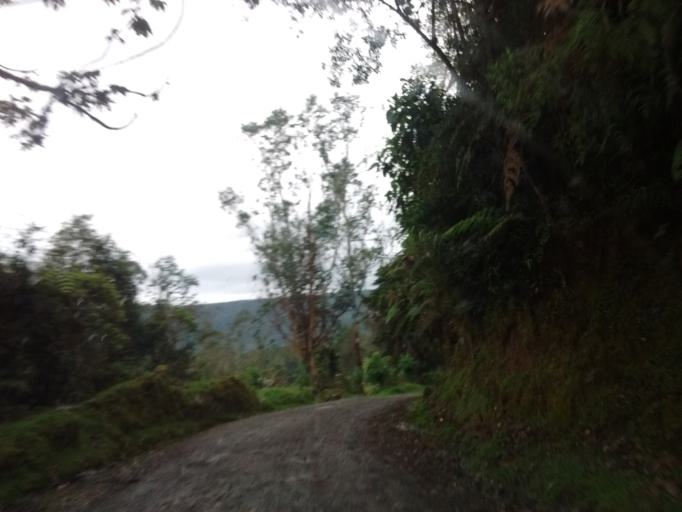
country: CO
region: Huila
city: La Argentina
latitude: 2.2609
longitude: -76.1963
